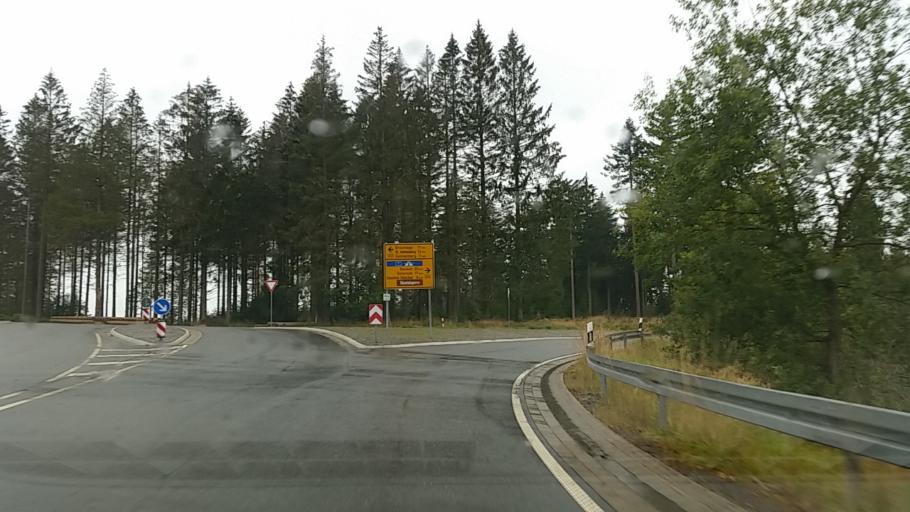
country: DE
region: Lower Saxony
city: Altenau
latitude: 51.7757
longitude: 10.4234
